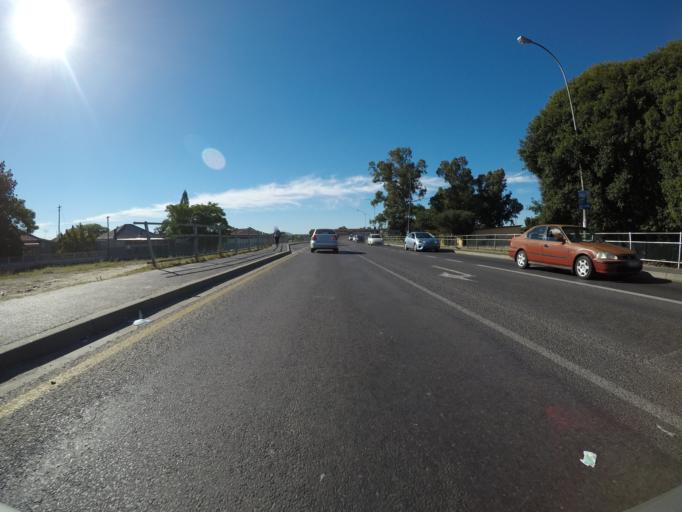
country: ZA
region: Western Cape
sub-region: City of Cape Town
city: Kraaifontein
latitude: -33.9343
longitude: 18.6762
